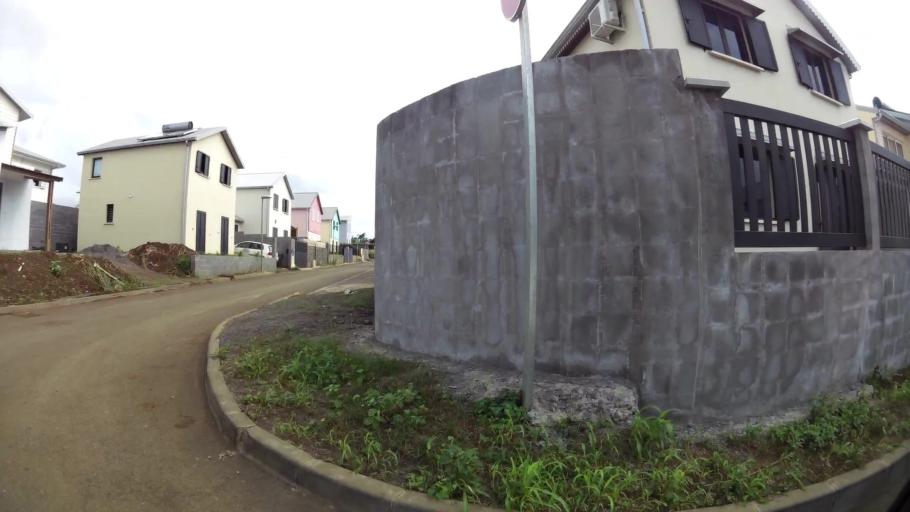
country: RE
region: Reunion
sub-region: Reunion
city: Sainte-Marie
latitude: -20.9030
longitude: 55.5711
